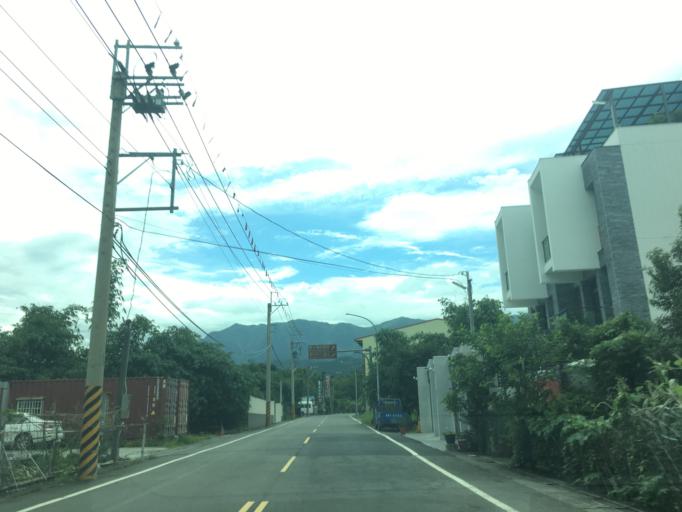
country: TW
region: Taiwan
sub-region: Yunlin
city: Douliu
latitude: 23.5898
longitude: 120.5534
